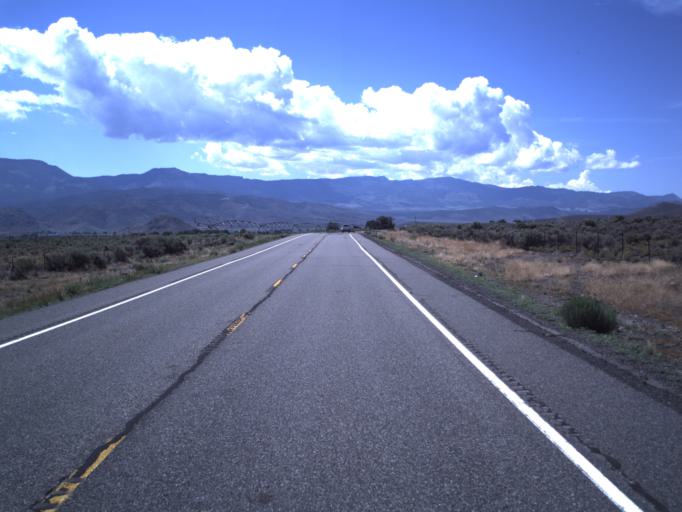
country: US
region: Utah
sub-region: Piute County
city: Junction
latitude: 38.2613
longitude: -112.2210
